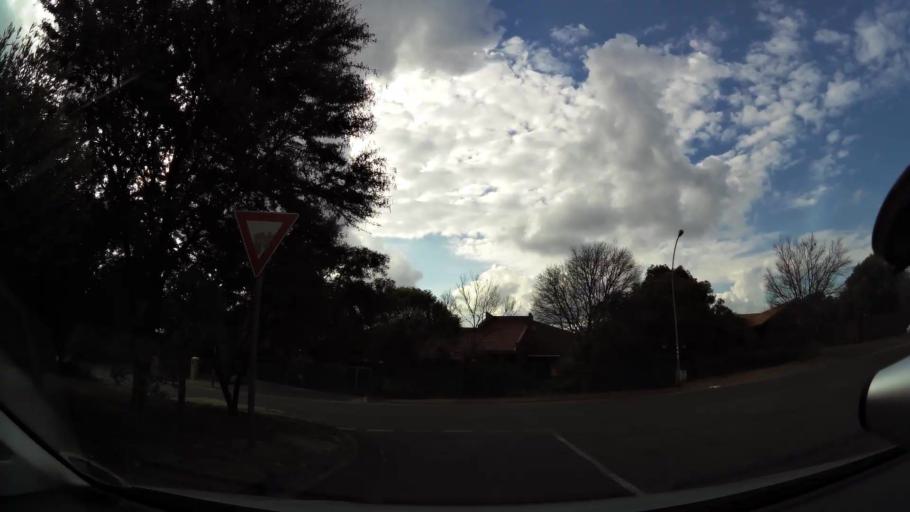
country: ZA
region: Orange Free State
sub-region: Mangaung Metropolitan Municipality
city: Bloemfontein
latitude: -29.0883
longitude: 26.1995
